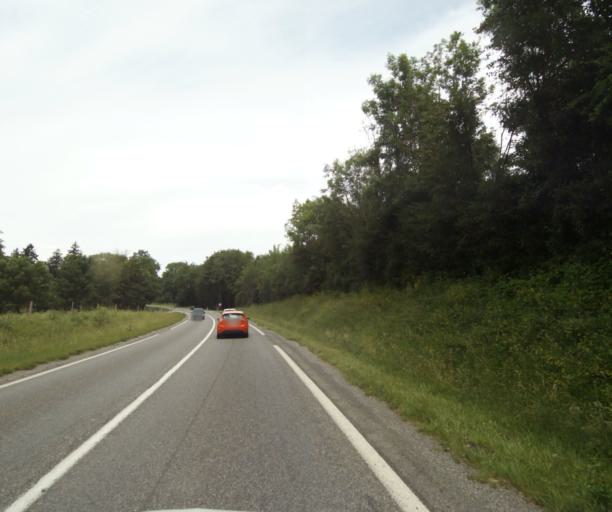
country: FR
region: Rhone-Alpes
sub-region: Departement de la Haute-Savoie
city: Allinges
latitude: 46.3428
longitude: 6.4641
